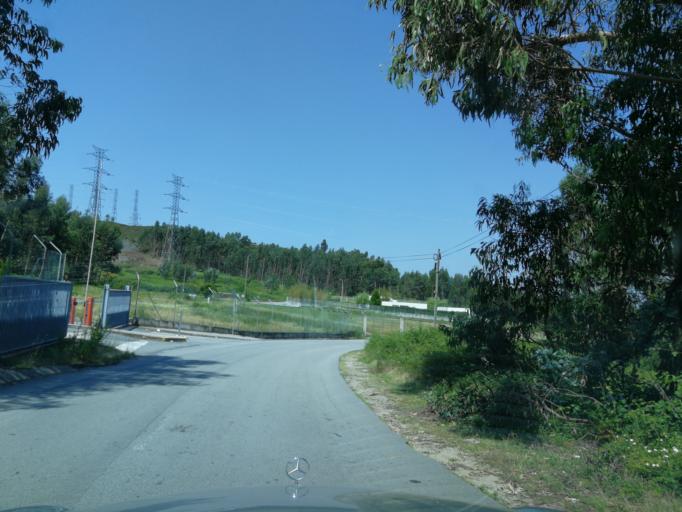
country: PT
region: Braga
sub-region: Povoa de Lanhoso
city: Povoa de Lanhoso
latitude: 41.5812
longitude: -8.3159
